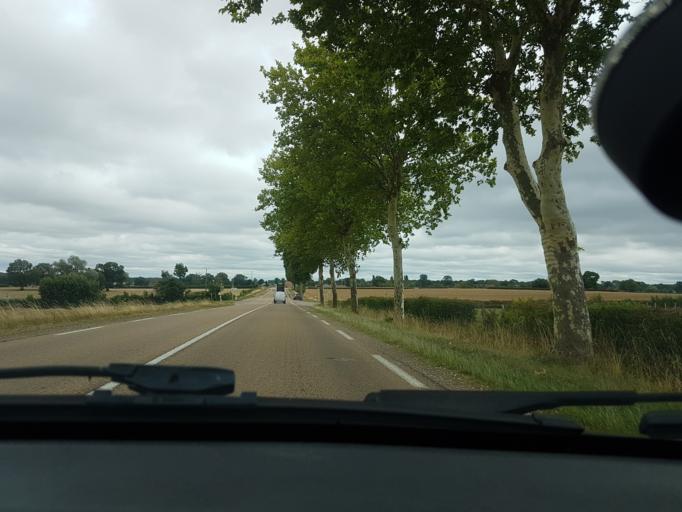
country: FR
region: Bourgogne
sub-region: Departement de l'Yonne
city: Avallon
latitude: 47.4886
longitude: 3.9842
